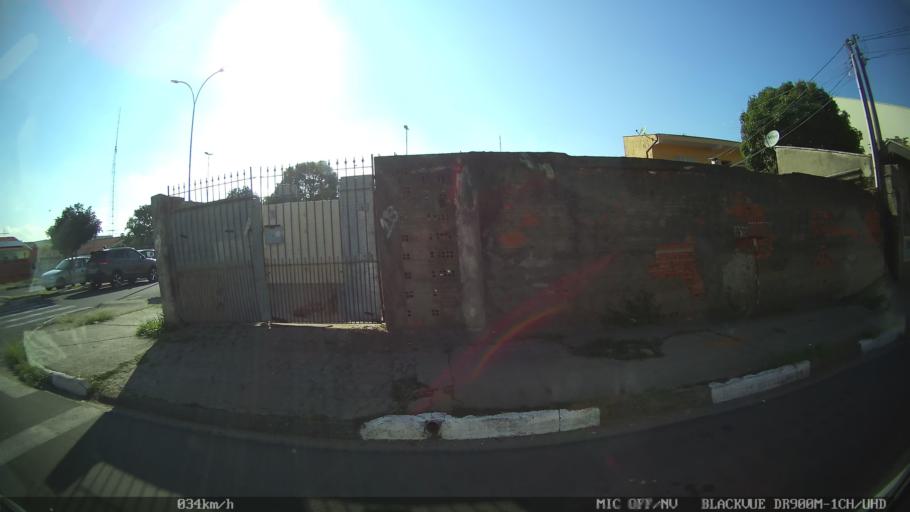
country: BR
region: Sao Paulo
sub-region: Hortolandia
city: Hortolandia
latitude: -22.8966
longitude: -47.1757
